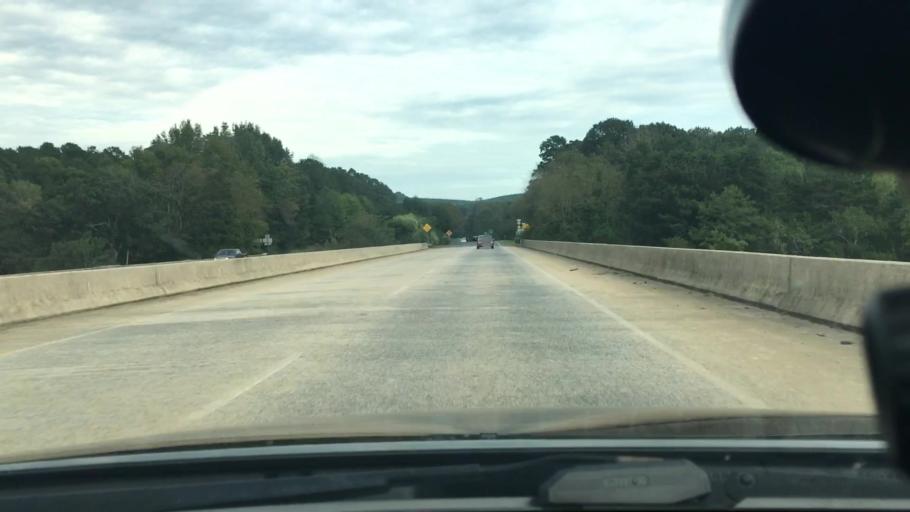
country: US
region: North Carolina
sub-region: Stanly County
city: Norwood
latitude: 35.3081
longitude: -80.0791
